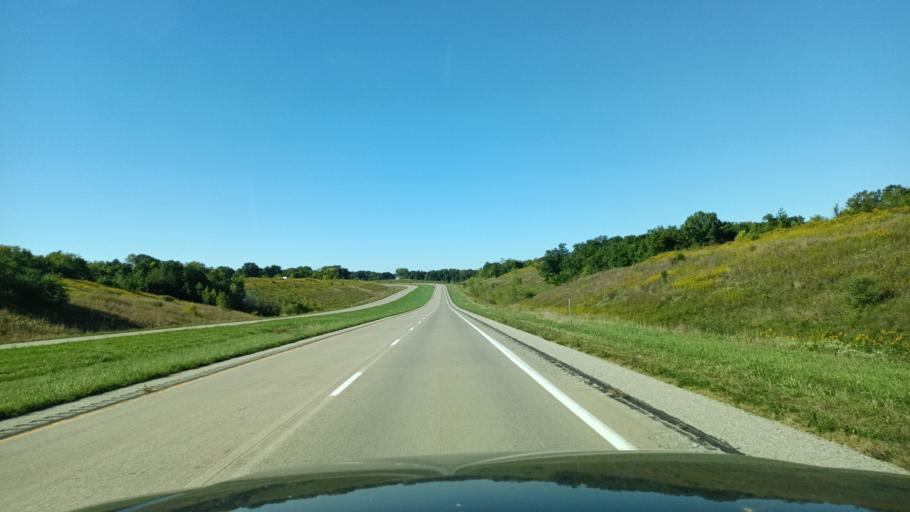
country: US
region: Iowa
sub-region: Lee County
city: Fort Madison
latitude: 40.6472
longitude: -91.3704
